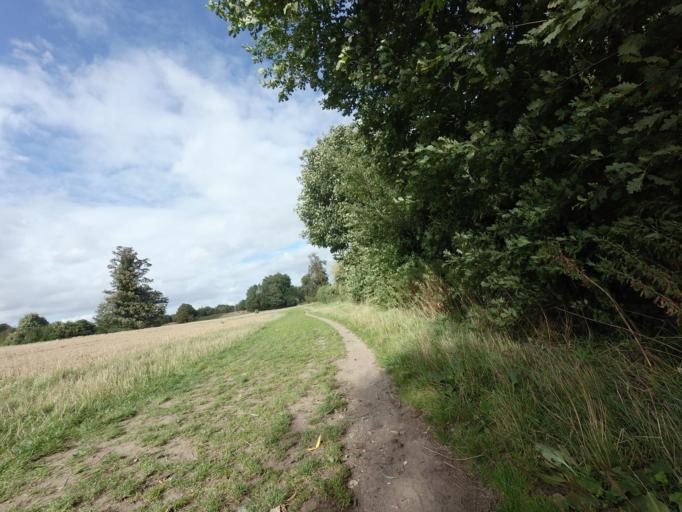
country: GB
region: England
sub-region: Kent
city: Eynsford
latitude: 51.3574
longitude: 0.1937
